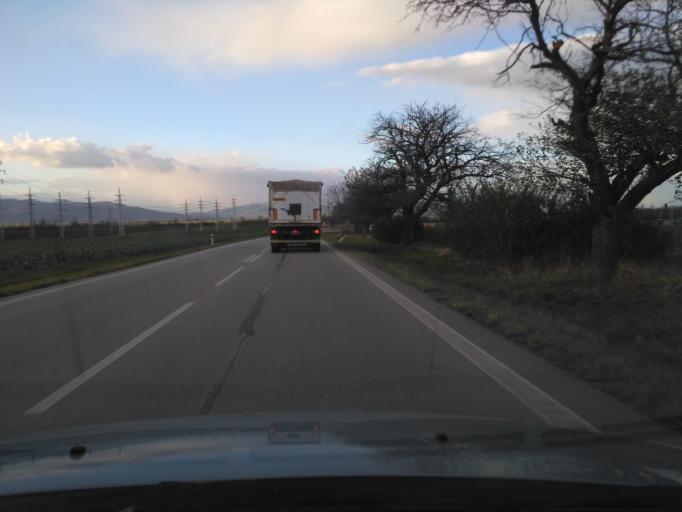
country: SK
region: Kosicky
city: Trebisov
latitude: 48.6316
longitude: 21.6923
